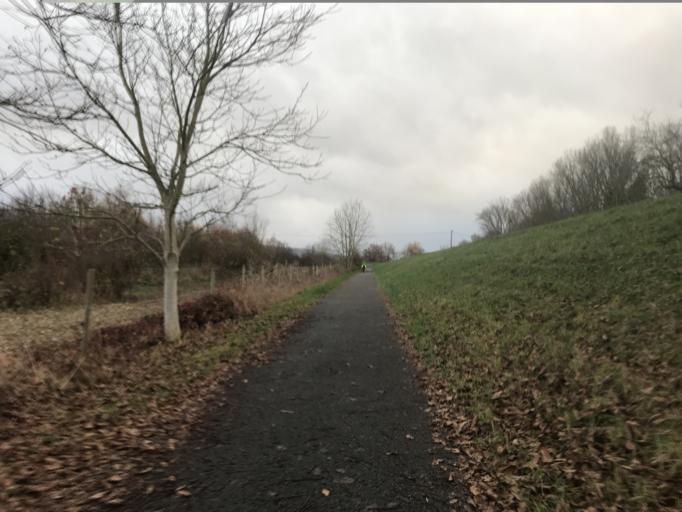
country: DE
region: Rheinland-Pfalz
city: Oestrich-Winkel
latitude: 49.9875
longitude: 8.0144
